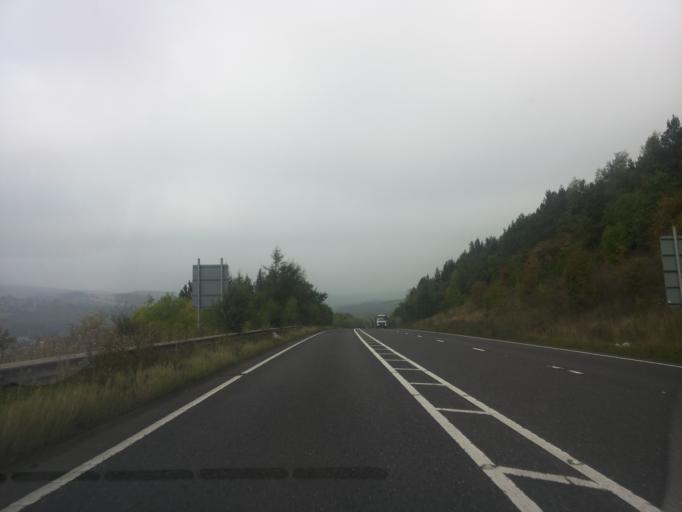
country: GB
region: England
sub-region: Sheffield
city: Stocksbridge
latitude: 53.4891
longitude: -1.6067
